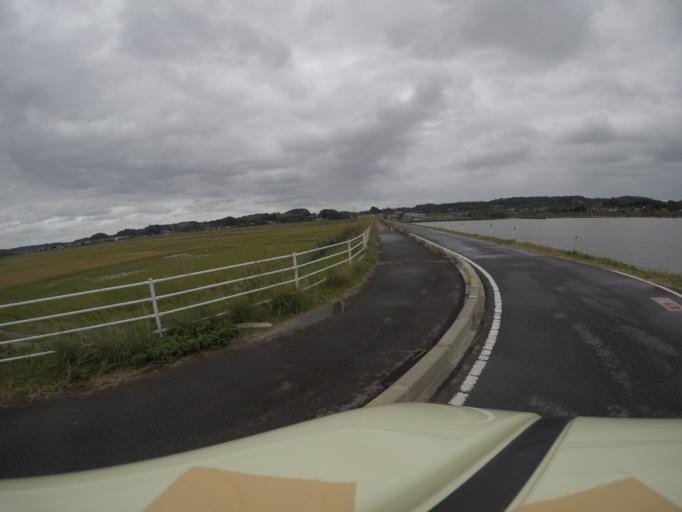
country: JP
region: Ibaraki
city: Itako
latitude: 36.0122
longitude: 140.4621
